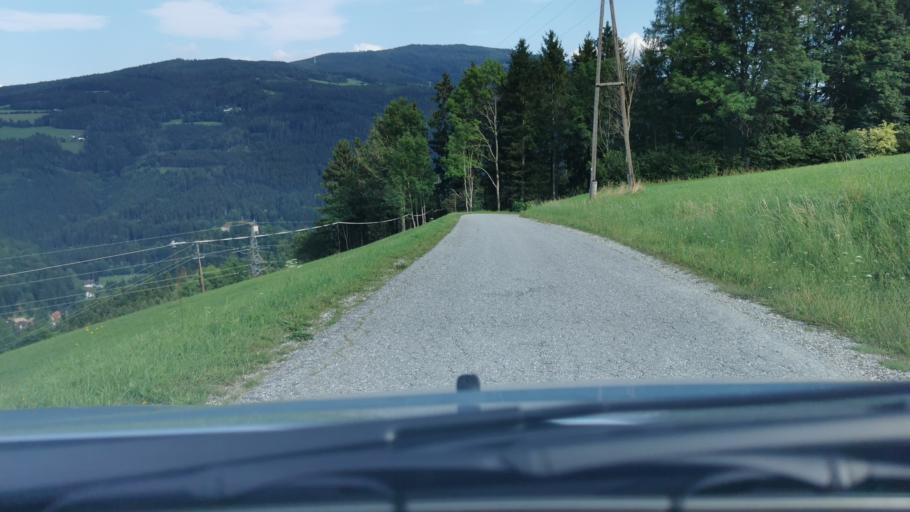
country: AT
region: Styria
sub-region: Politischer Bezirk Weiz
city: Koglhof
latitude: 47.3128
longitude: 15.6761
